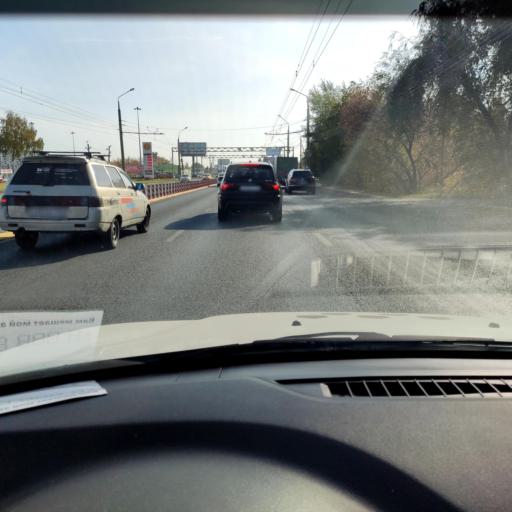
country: RU
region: Samara
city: Tol'yatti
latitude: 53.5427
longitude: 49.3836
